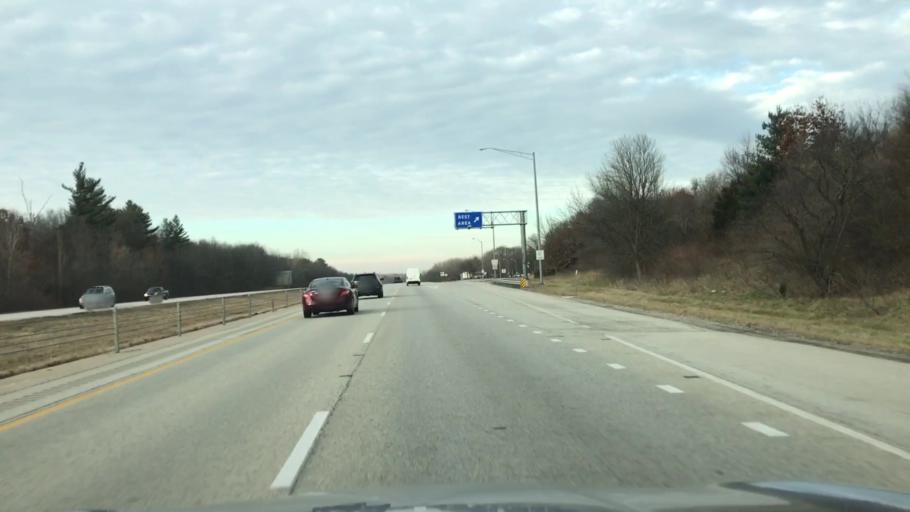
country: US
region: Illinois
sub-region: Sangamon County
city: Sherman
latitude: 39.8611
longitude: -89.5953
